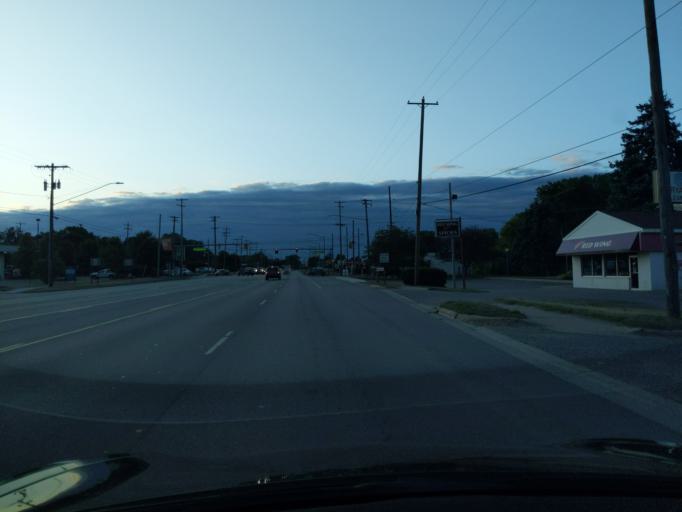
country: US
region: Michigan
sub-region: Ingham County
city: Holt
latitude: 42.6539
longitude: -84.5317
